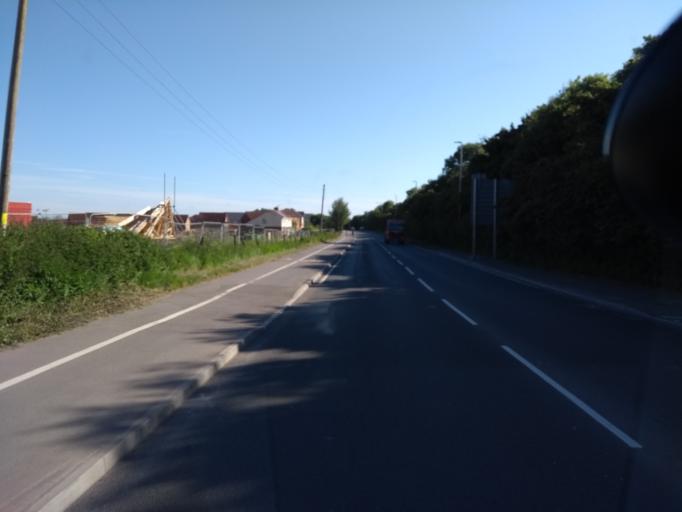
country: GB
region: England
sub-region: Somerset
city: North Petherton
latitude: 51.1053
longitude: -2.9967
